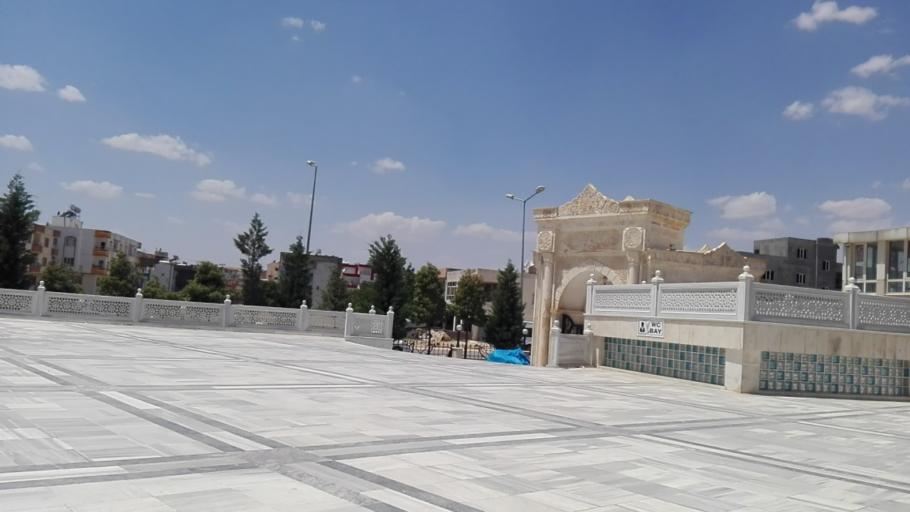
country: TR
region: Mardin
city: Midyat
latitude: 37.4192
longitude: 41.3617
